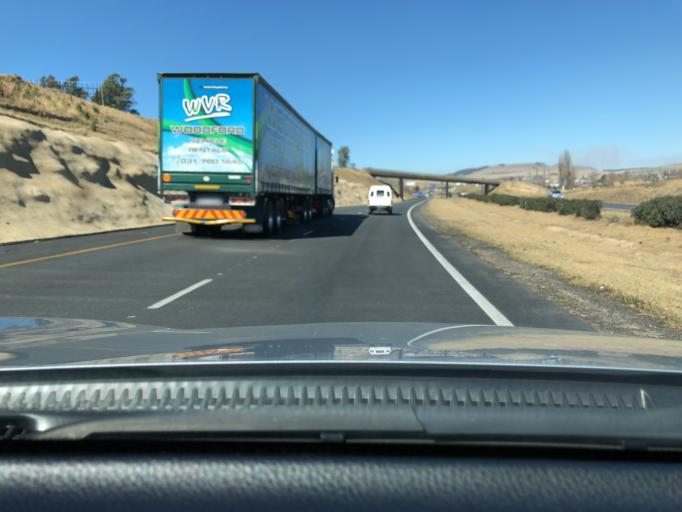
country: ZA
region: KwaZulu-Natal
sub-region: uMgungundlovu District Municipality
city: Mooirivier
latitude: -29.2024
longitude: 30.0010
